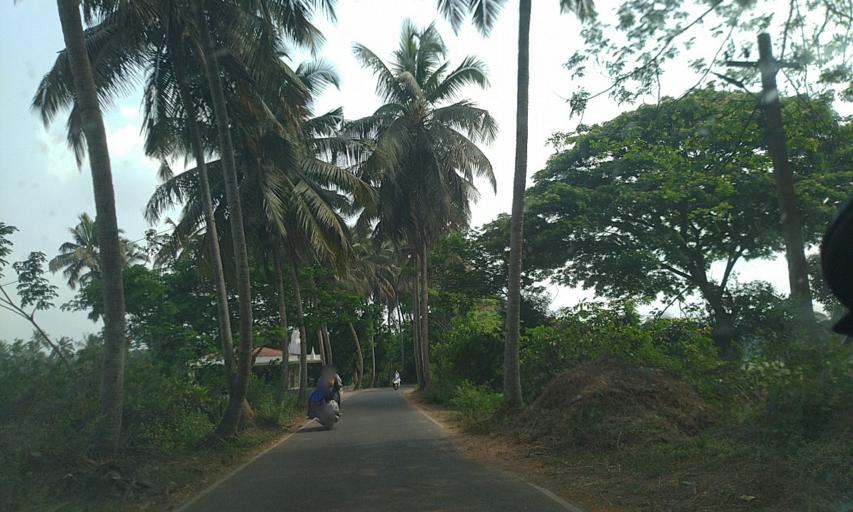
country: IN
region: Goa
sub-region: North Goa
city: Taleigao
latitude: 15.4724
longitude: 73.8412
